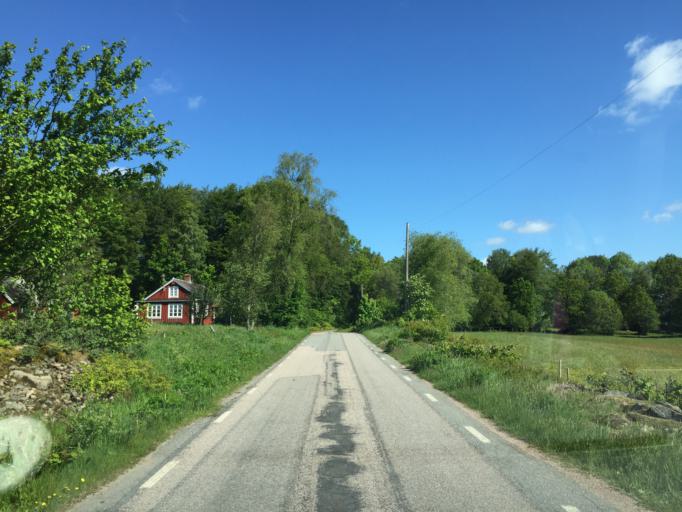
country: SE
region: Kronoberg
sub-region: Markaryds Kommun
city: Stromsnasbruk
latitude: 56.5889
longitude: 13.6008
